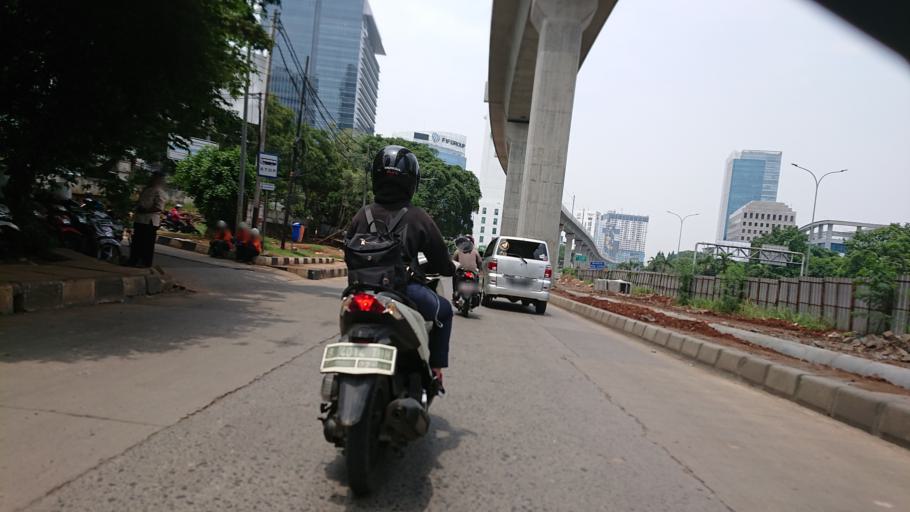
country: ID
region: Banten
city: South Tangerang
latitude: -6.2925
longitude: 106.7873
